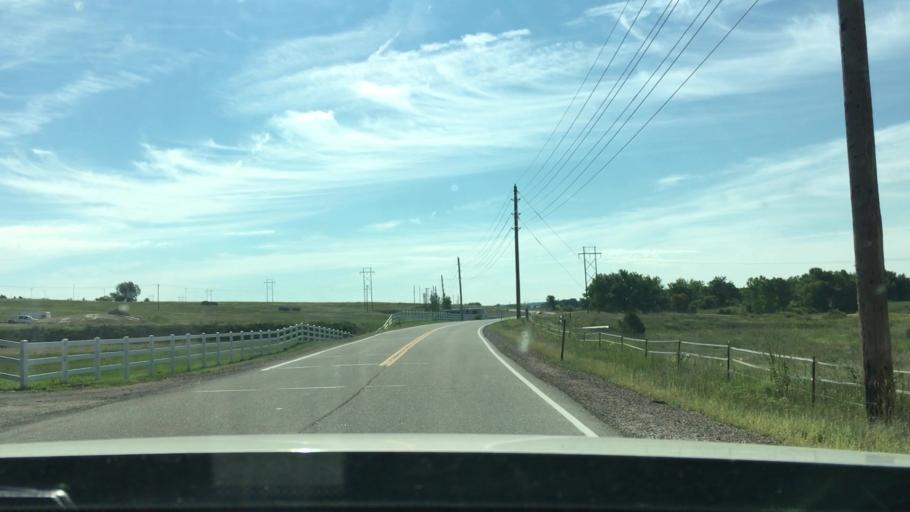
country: US
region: Colorado
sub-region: Douglas County
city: The Pinery
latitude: 39.4310
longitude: -104.7463
